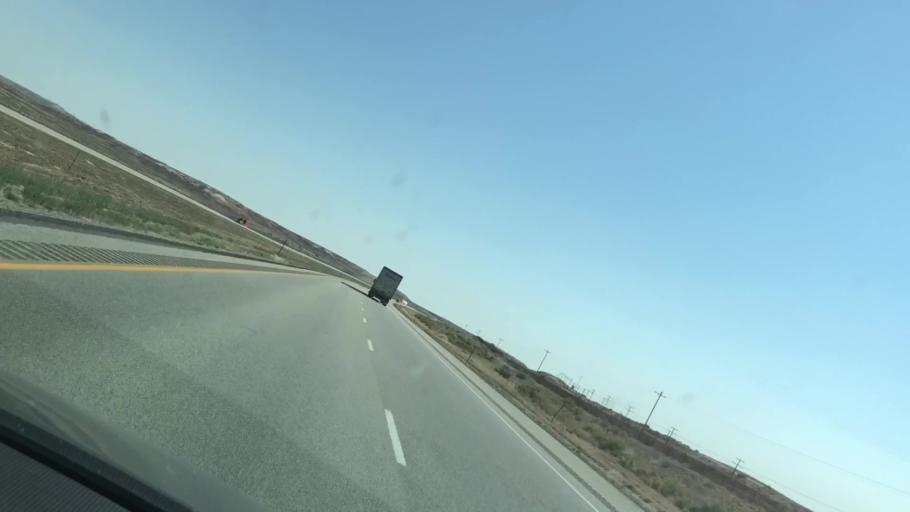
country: US
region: Wyoming
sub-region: Carbon County
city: Rawlins
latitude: 41.7032
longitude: -107.8998
